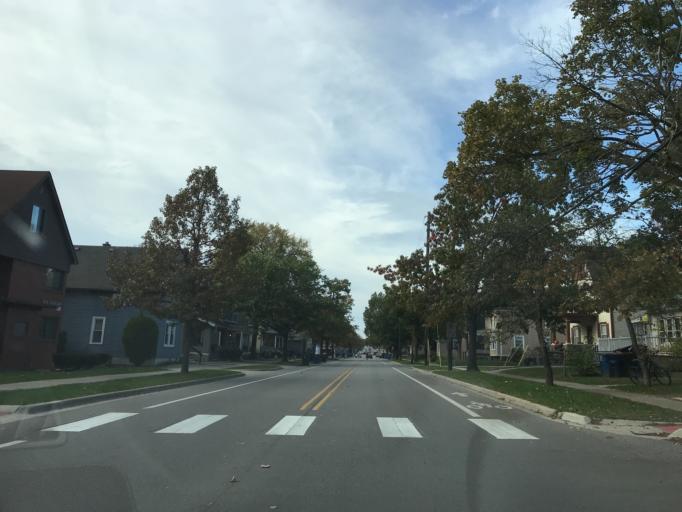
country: US
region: Michigan
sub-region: Washtenaw County
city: Ann Arbor
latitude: 42.2684
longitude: -83.7379
